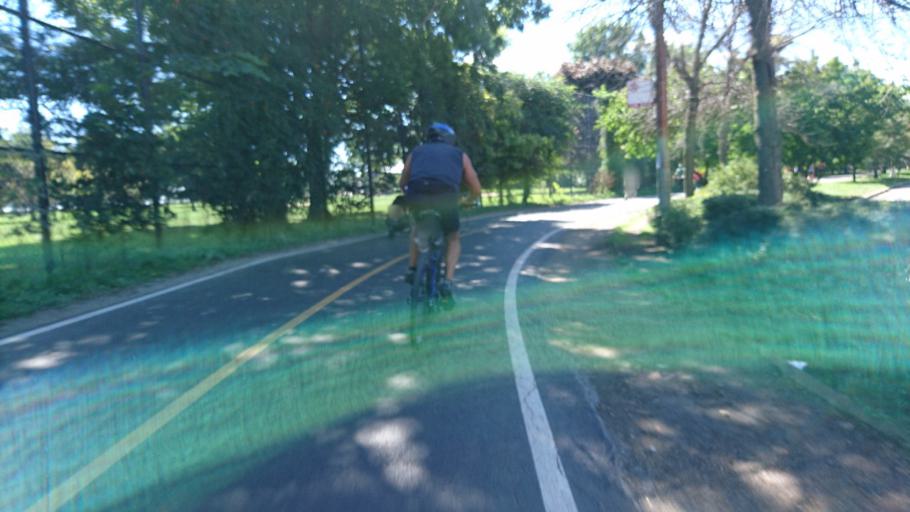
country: US
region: Illinois
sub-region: Cook County
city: Evanston
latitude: 41.9548
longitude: -87.6438
